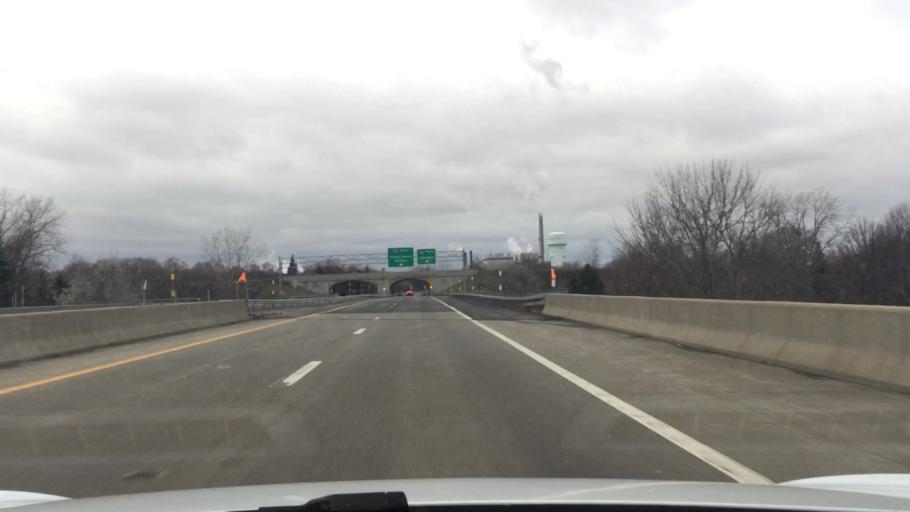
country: US
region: New York
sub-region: Niagara County
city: Niagara Falls
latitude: 43.0806
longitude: -78.9872
